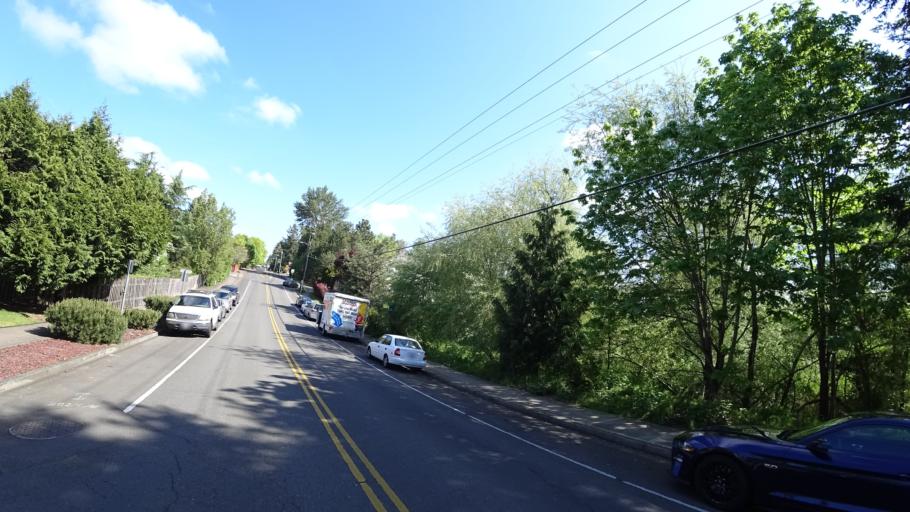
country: US
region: Oregon
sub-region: Washington County
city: King City
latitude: 45.4432
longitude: -122.8209
